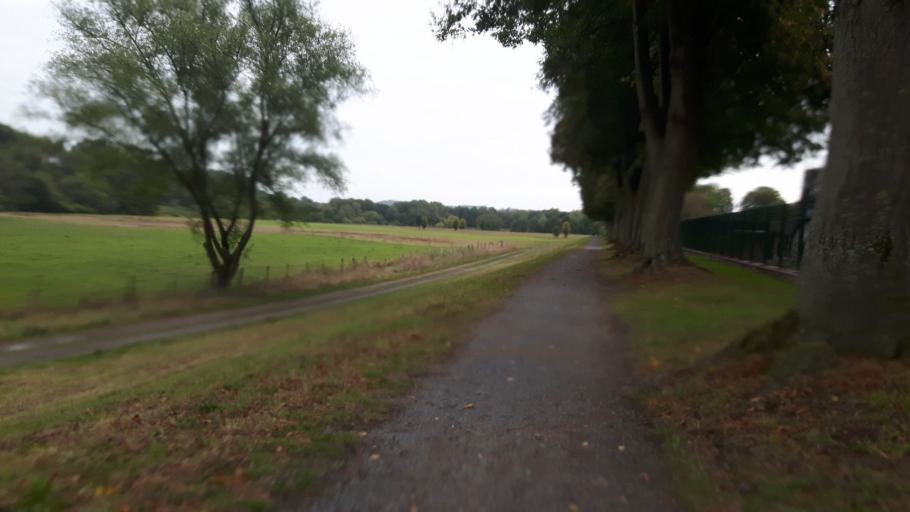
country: DE
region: North Rhine-Westphalia
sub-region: Regierungsbezirk Koln
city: Hennef
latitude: 50.7855
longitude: 7.2840
